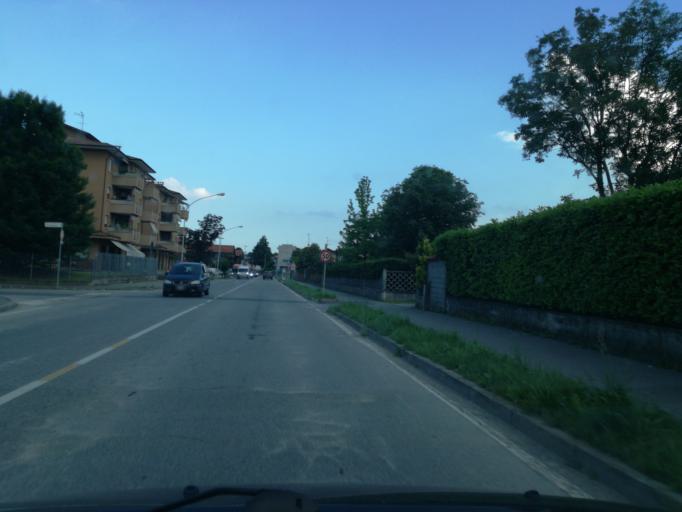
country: IT
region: Lombardy
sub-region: Provincia di Monza e Brianza
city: Porto d'Adda
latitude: 45.6479
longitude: 9.4634
